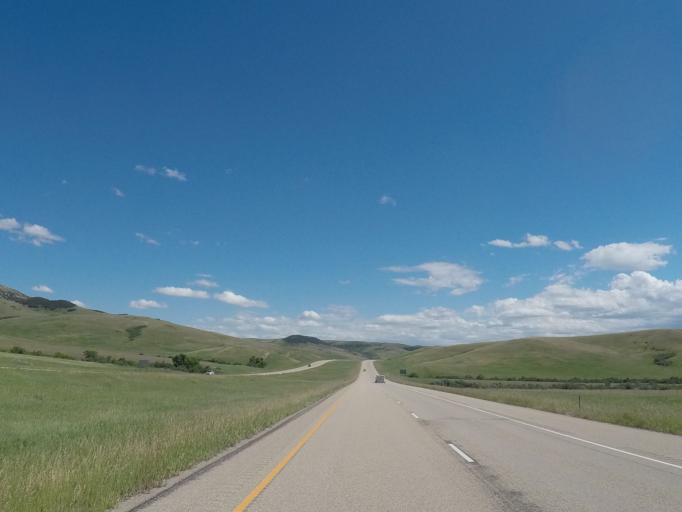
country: US
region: Wyoming
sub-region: Sheridan County
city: Sheridan
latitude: 45.0721
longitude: -107.3427
